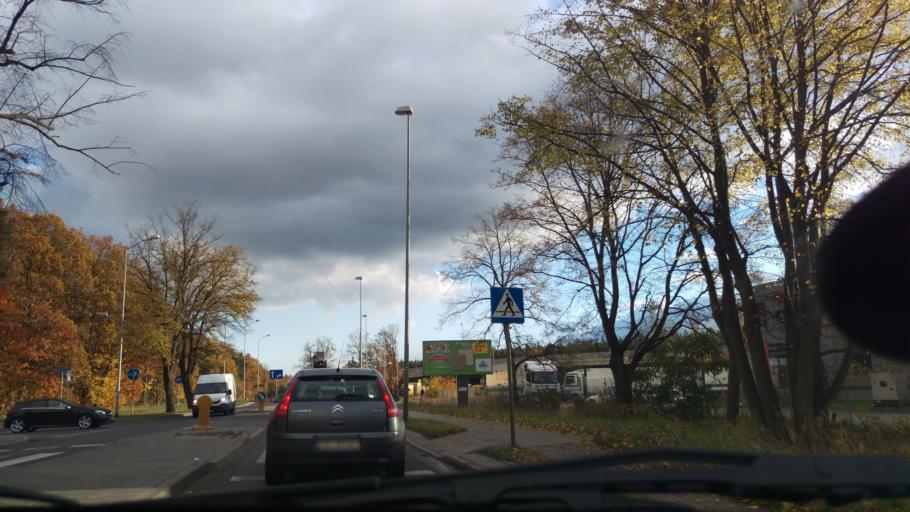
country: PL
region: West Pomeranian Voivodeship
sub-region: Szczecin
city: Szczecin
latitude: 53.3833
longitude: 14.6819
